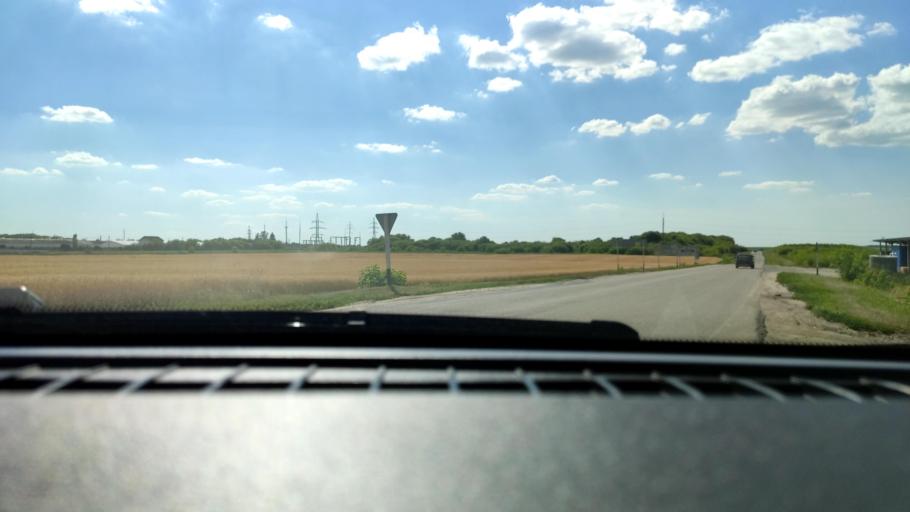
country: RU
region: Voronezj
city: Ramon'
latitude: 51.9338
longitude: 39.3471
